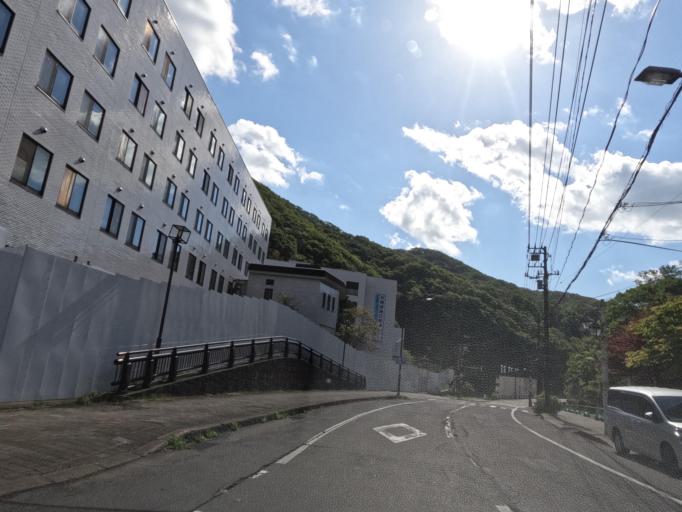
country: JP
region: Hokkaido
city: Shiraoi
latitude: 42.4887
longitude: 141.1474
